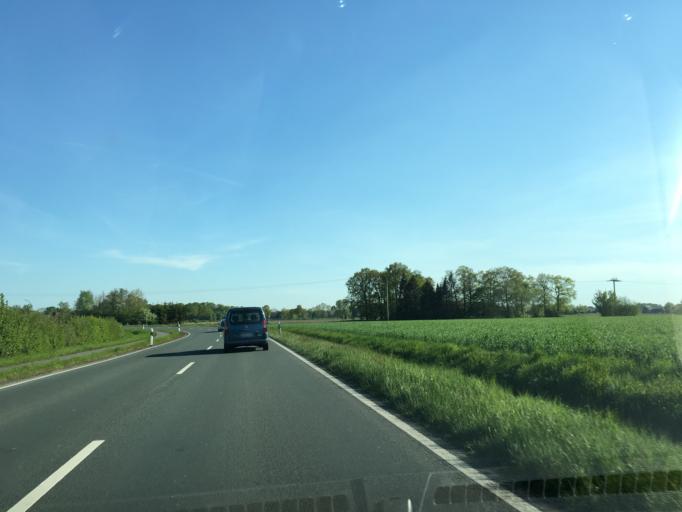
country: DE
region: North Rhine-Westphalia
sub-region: Regierungsbezirk Munster
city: Senden
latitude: 51.8329
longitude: 7.5200
